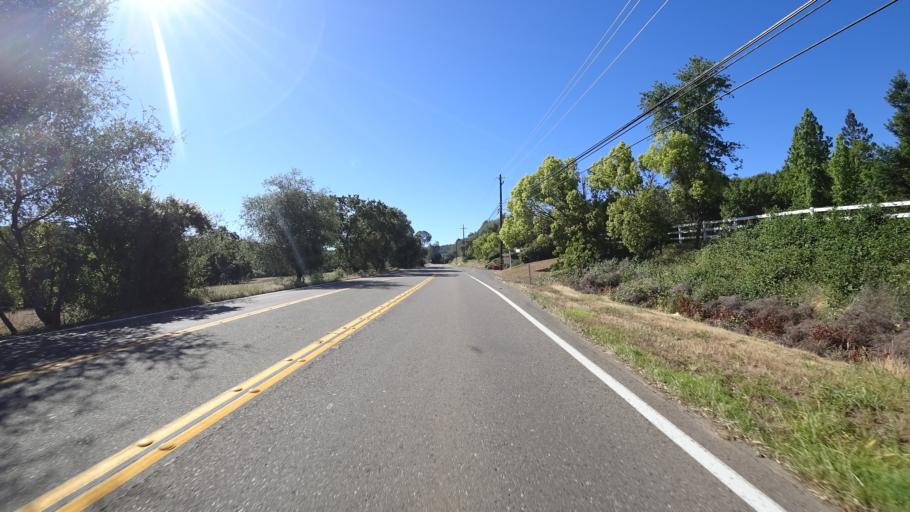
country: US
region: California
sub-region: Placer County
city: Newcastle
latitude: 38.8886
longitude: -121.1778
